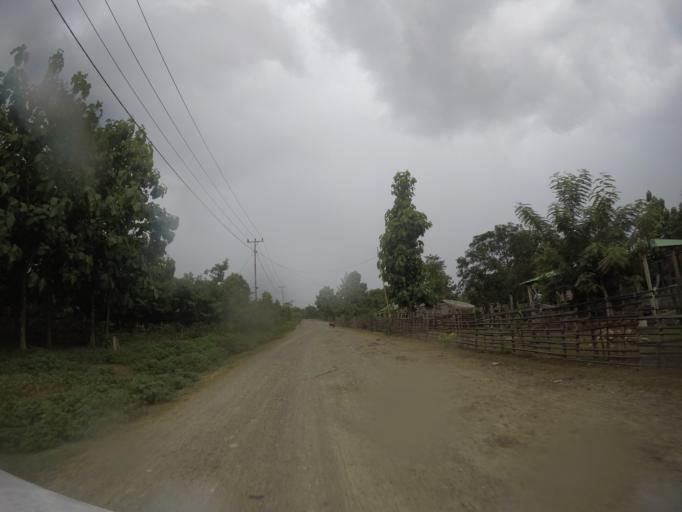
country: TL
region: Bobonaro
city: Maliana
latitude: -8.8514
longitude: 125.0865
